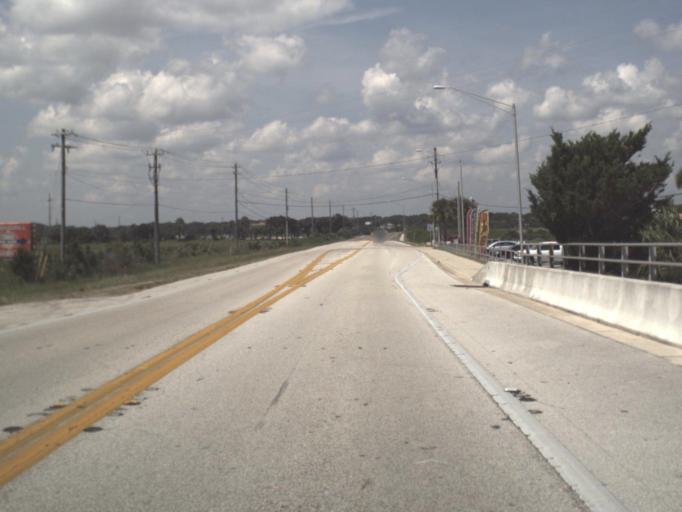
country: US
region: Florida
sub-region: Saint Johns County
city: Saint Augustine
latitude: 29.9155
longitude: -81.3066
